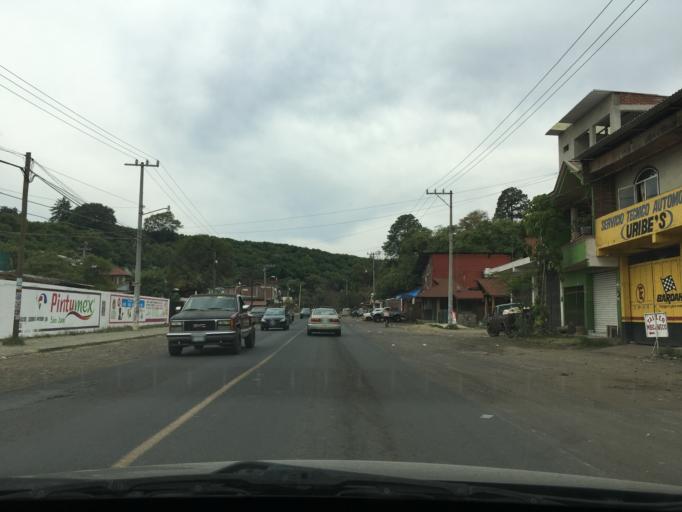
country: MX
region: Michoacan
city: Nuevo San Juan Parangaricutiro
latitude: 19.4135
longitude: -102.1203
